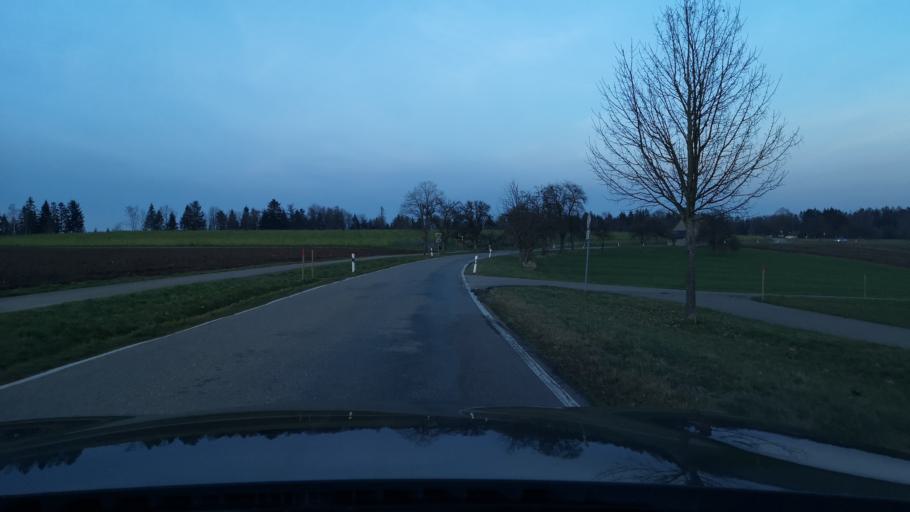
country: DE
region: Baden-Wuerttemberg
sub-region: Regierungsbezirk Stuttgart
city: Kaisersbach
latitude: 48.9339
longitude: 9.6390
